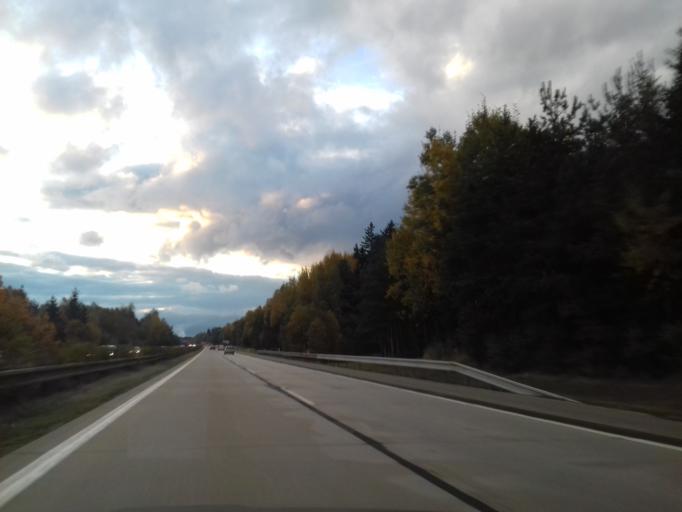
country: CZ
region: Vysocina
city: Luka nad Jihlavou
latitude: 49.4100
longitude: 15.7429
